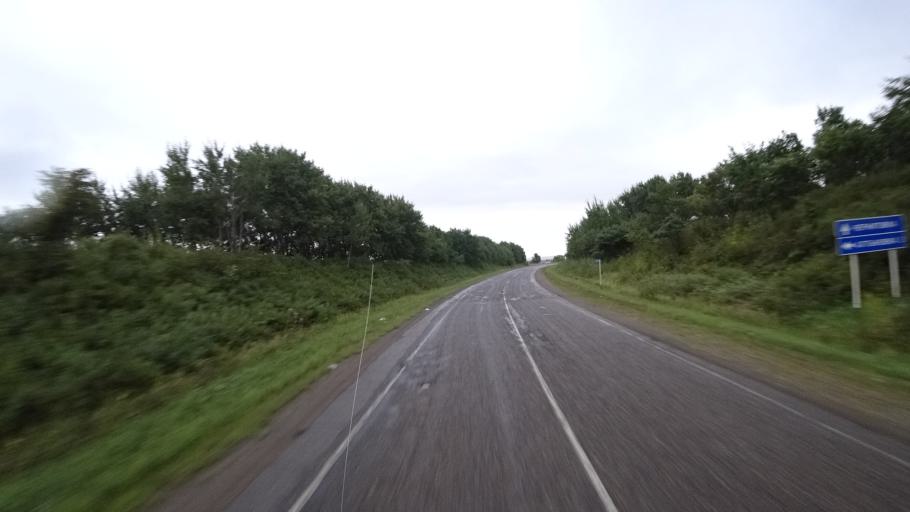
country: RU
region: Primorskiy
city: Chernigovka
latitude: 44.3666
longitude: 132.5313
